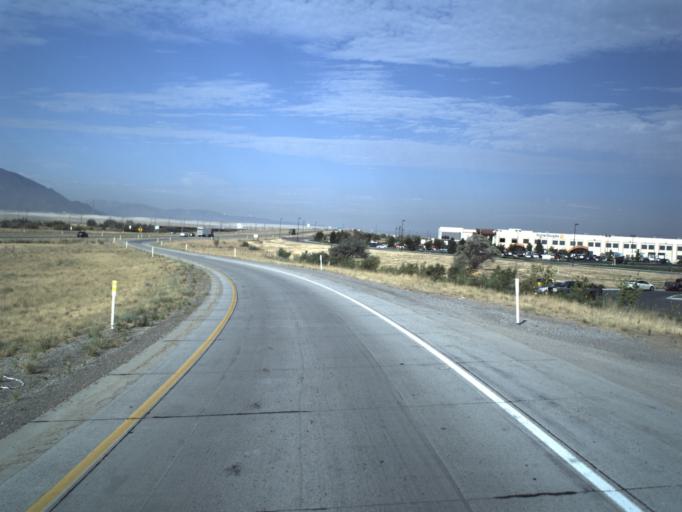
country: US
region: Utah
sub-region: Salt Lake County
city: West Valley City
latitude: 40.7721
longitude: -112.0262
